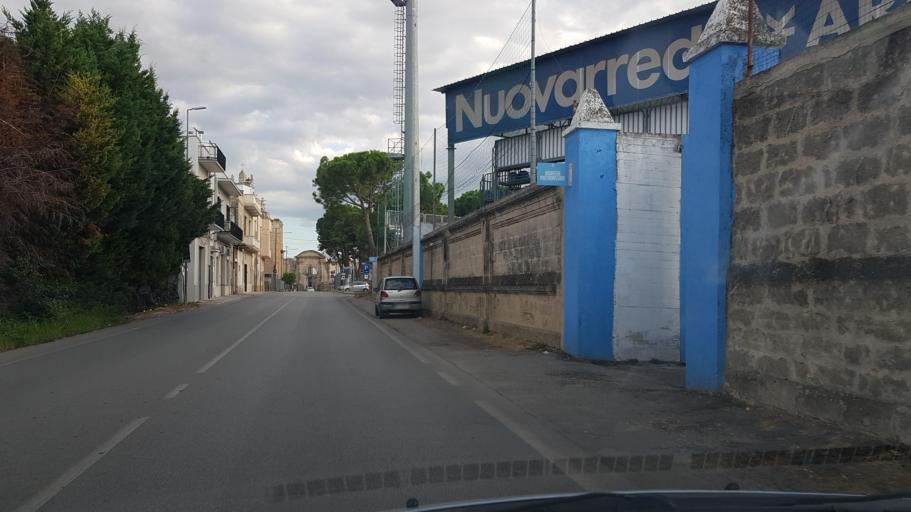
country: IT
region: Apulia
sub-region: Provincia di Brindisi
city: Francavilla Fontana
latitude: 40.5356
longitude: 17.5779
